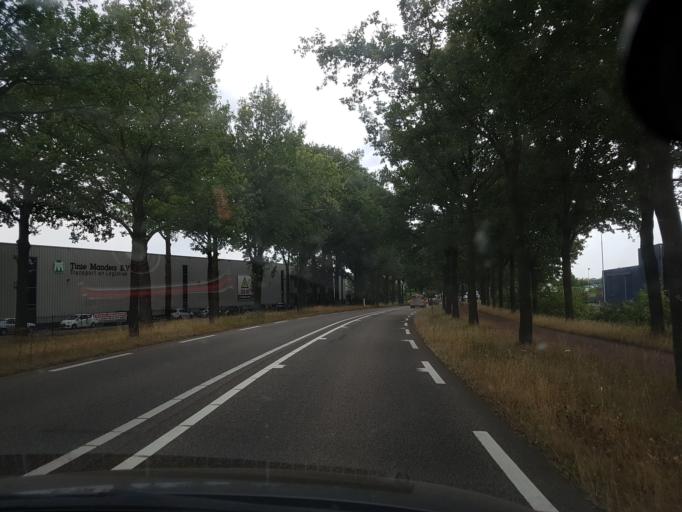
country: NL
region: North Brabant
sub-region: Gemeente Geldrop-Mierlo
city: Geldrop
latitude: 51.4397
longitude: 5.5645
